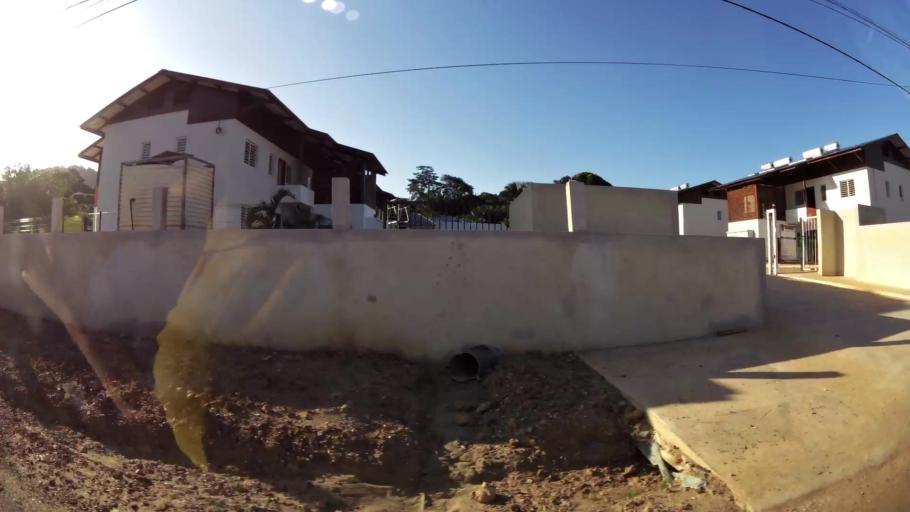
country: GF
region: Guyane
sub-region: Guyane
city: Remire-Montjoly
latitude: 4.8888
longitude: -52.2908
